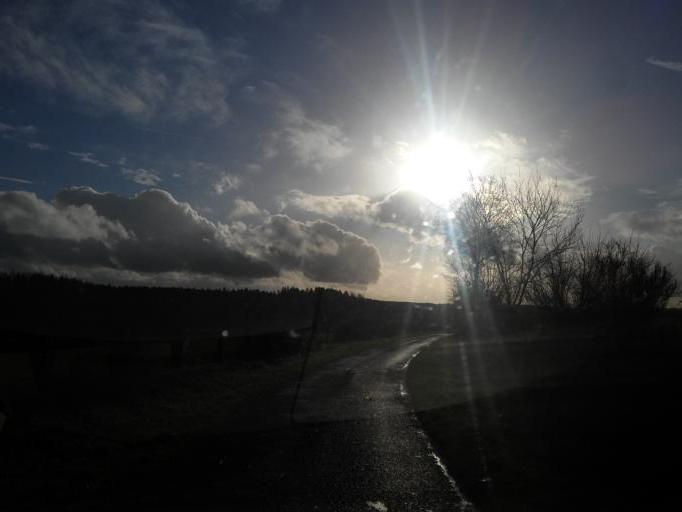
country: BE
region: Wallonia
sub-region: Province du Luxembourg
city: Neufchateau
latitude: 49.8093
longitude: 5.4411
